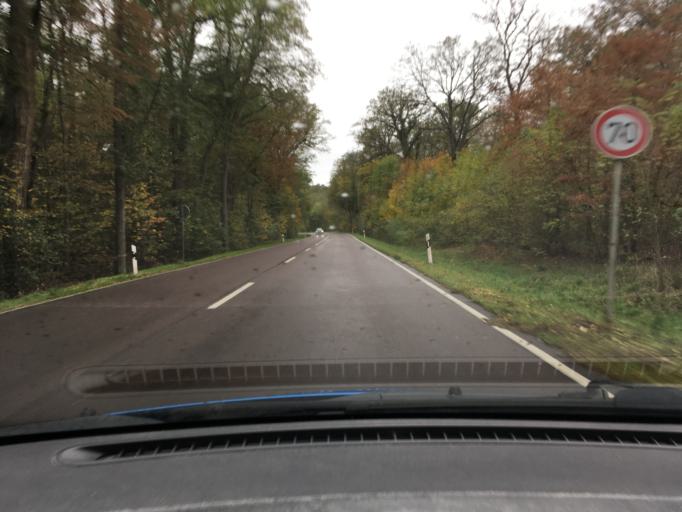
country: DE
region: Saxony-Anhalt
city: Vockerode
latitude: 51.8882
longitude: 12.3147
